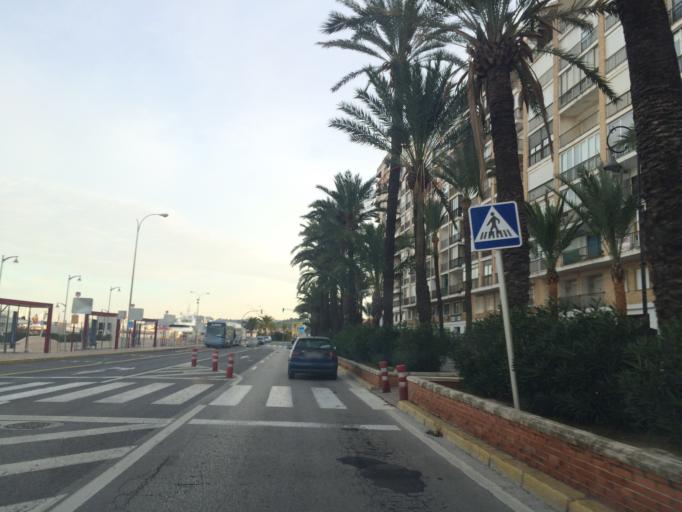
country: ES
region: Valencia
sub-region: Provincia de Alicante
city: Denia
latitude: 38.8425
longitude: 0.1118
